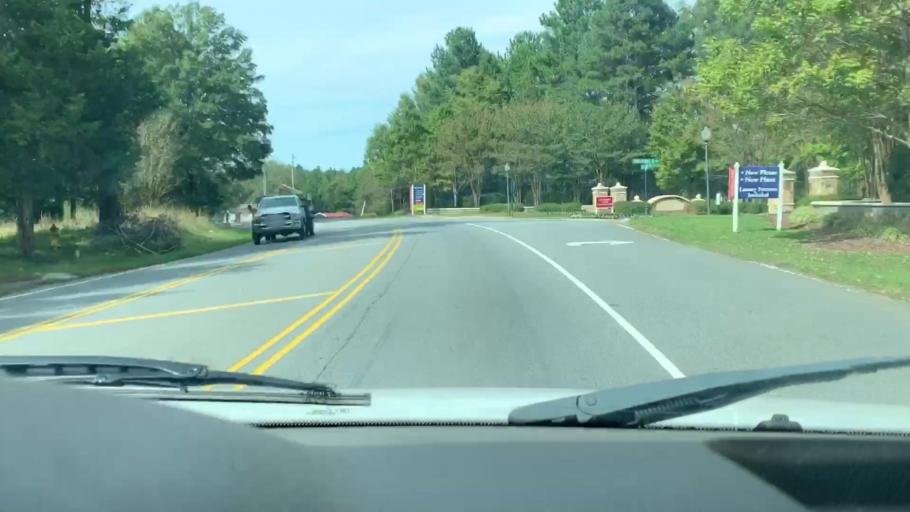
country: US
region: North Carolina
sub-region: Mecklenburg County
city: Huntersville
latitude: 35.4300
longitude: -80.7578
